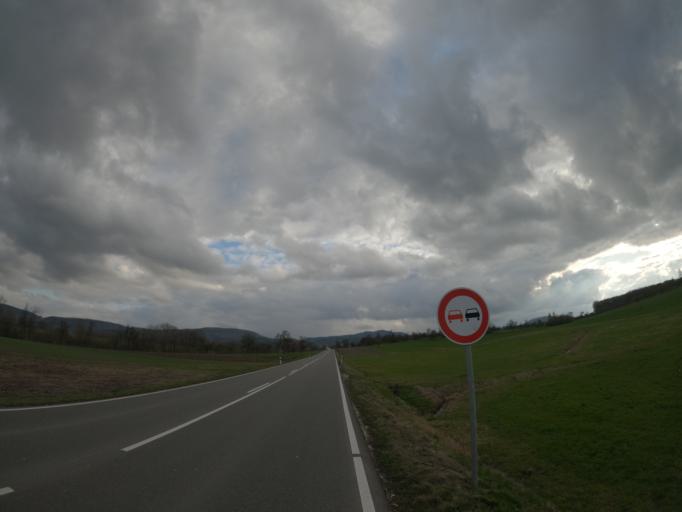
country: DE
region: Baden-Wuerttemberg
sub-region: Regierungsbezirk Stuttgart
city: Boll
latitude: 48.6617
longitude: 9.6145
